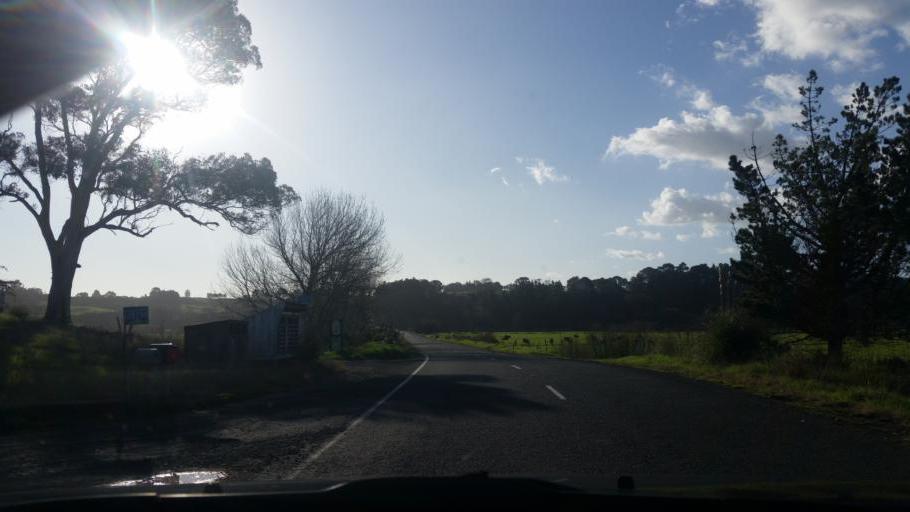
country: NZ
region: Northland
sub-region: Kaipara District
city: Dargaville
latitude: -36.1450
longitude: 173.9841
